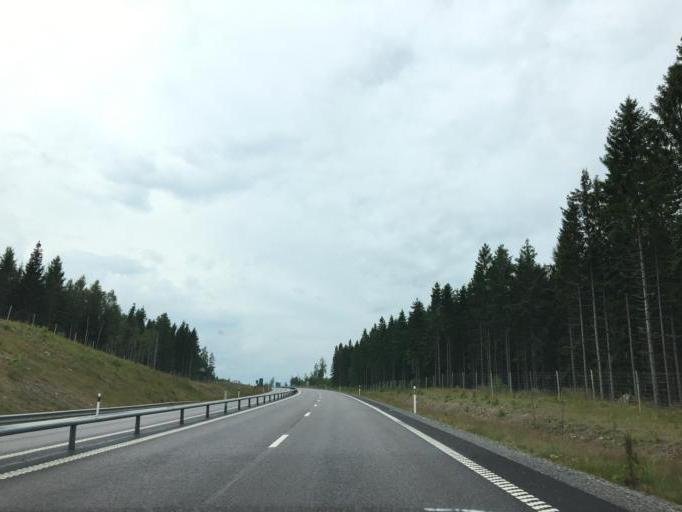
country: SE
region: Soedermanland
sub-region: Katrineholms Kommun
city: Katrineholm
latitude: 58.9563
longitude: 16.2239
